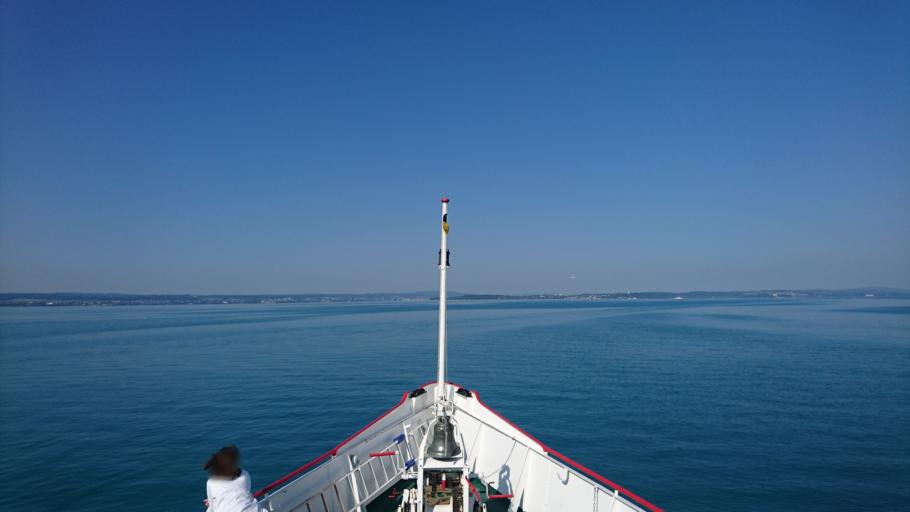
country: DE
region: Baden-Wuerttemberg
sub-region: Tuebingen Region
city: Hagnau
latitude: 47.6715
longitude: 9.3080
